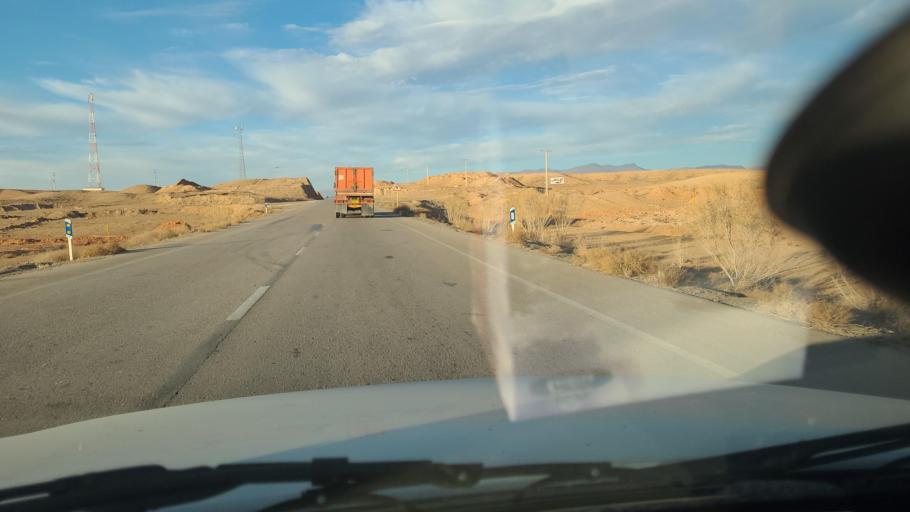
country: IR
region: Razavi Khorasan
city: Neqab
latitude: 36.7726
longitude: 57.5875
